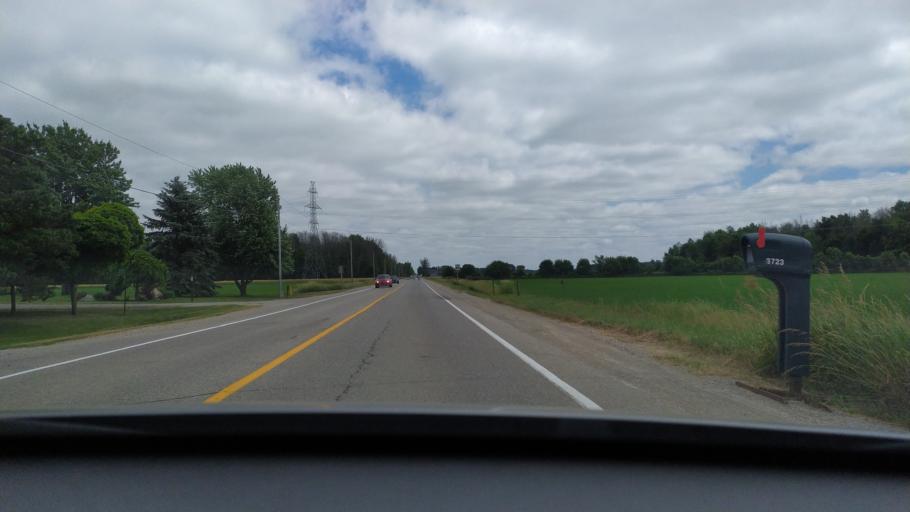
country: CA
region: Ontario
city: Stratford
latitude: 43.3459
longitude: -80.9683
